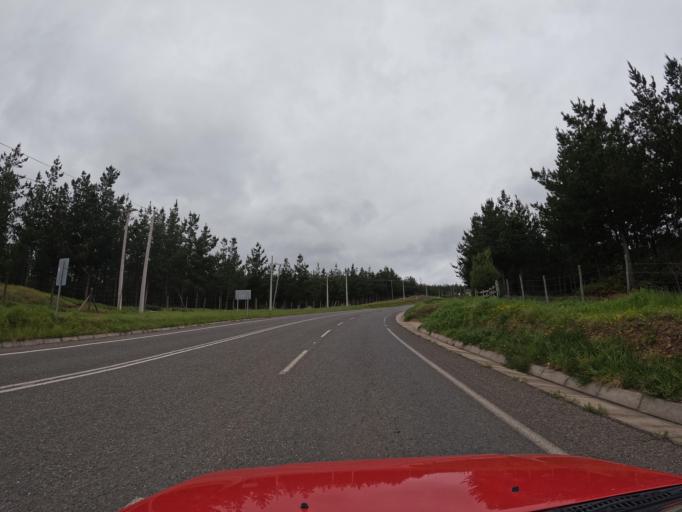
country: CL
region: O'Higgins
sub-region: Provincia de Colchagua
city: Santa Cruz
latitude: -34.6341
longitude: -72.0309
